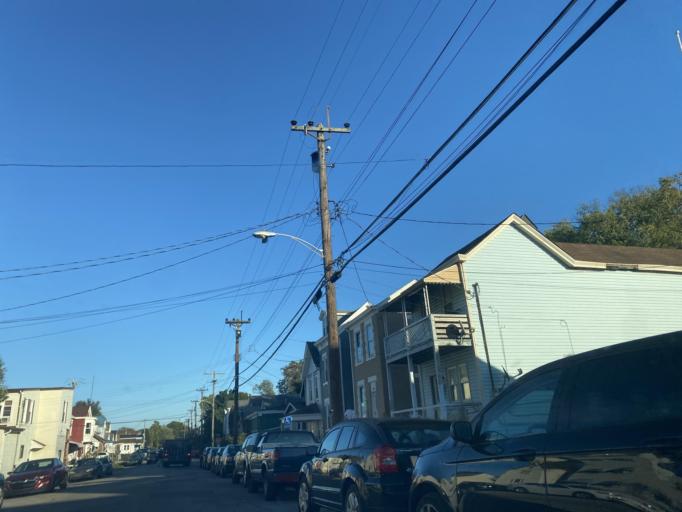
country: US
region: Kentucky
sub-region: Campbell County
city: Dayton
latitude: 39.1143
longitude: -84.4659
